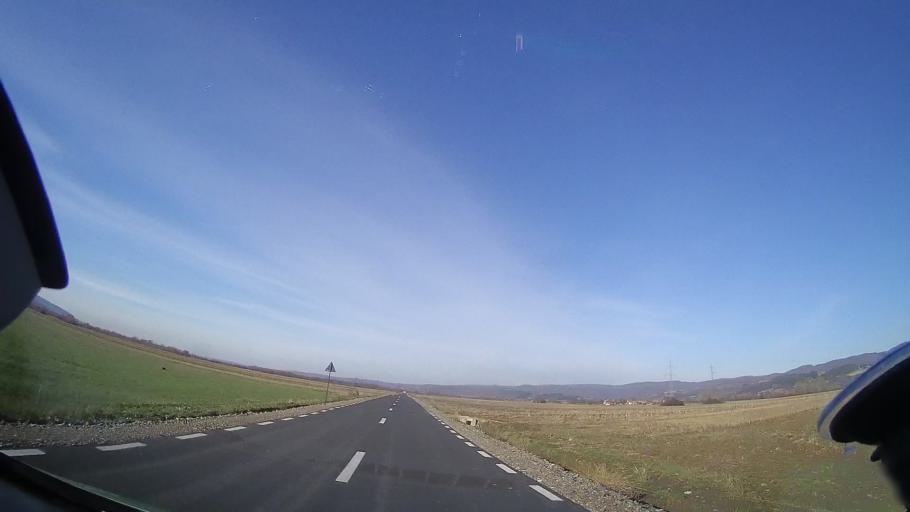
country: RO
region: Bihor
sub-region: Comuna Auseu
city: Auseu
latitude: 47.0130
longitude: 22.4972
